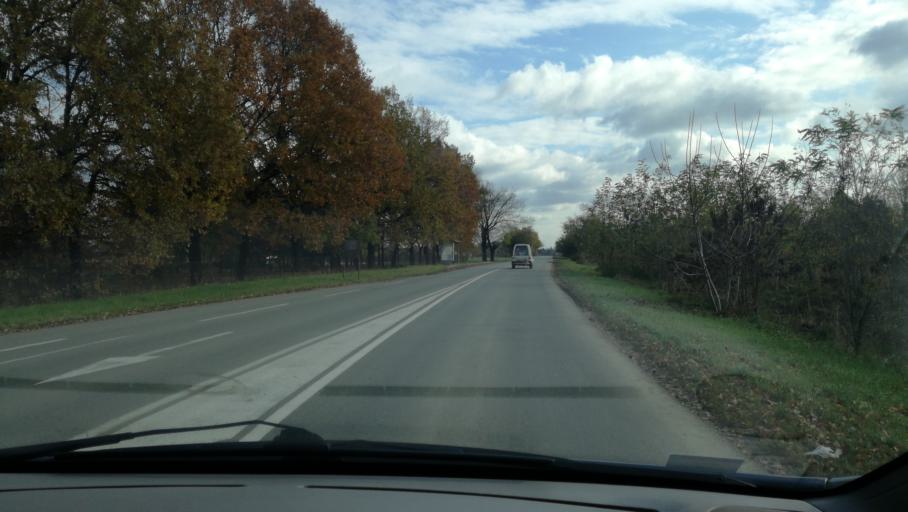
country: RS
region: Autonomna Pokrajina Vojvodina
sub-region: Severnobanatski Okrug
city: Kikinda
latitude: 45.8233
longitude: 20.4292
